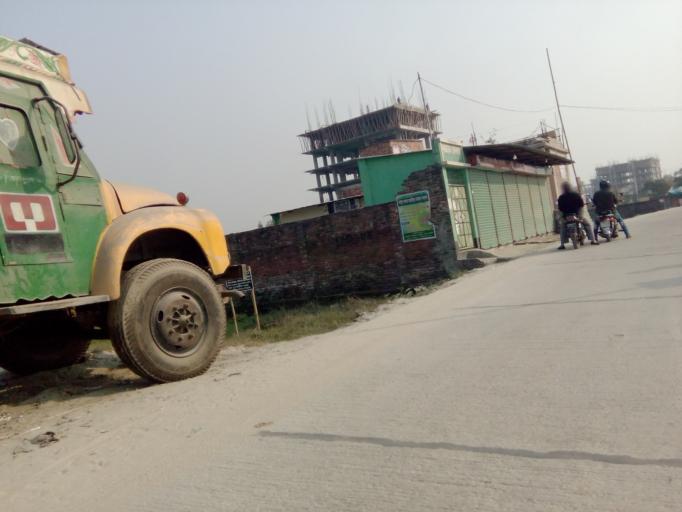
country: BD
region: Dhaka
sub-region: Dhaka
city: Dhaka
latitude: 23.7007
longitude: 90.4752
